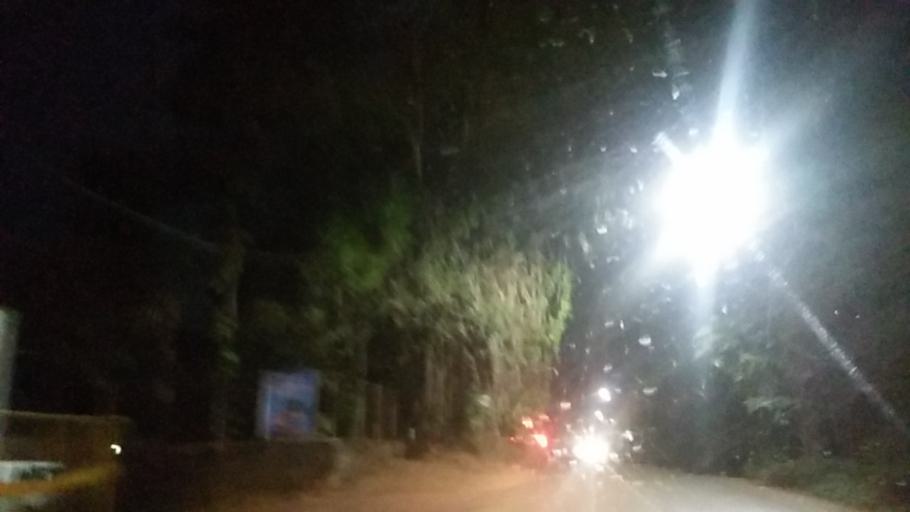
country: IN
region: Goa
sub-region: South Goa
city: Raia
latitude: 15.2987
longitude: 73.9699
